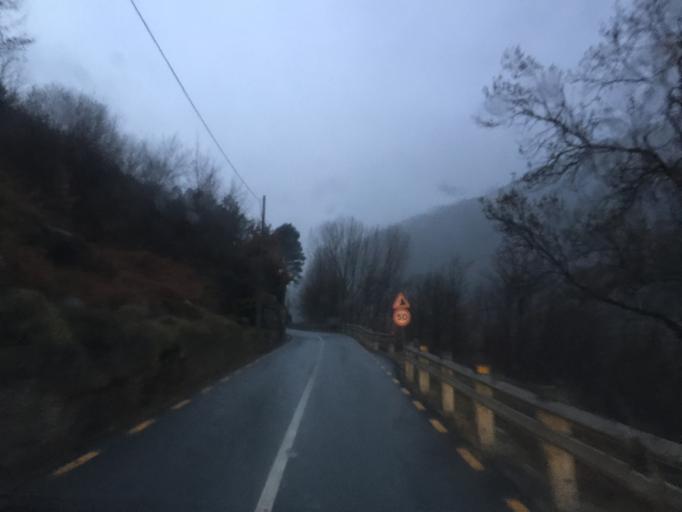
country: PT
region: Guarda
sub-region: Manteigas
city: Manteigas
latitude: 40.3812
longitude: -7.5445
